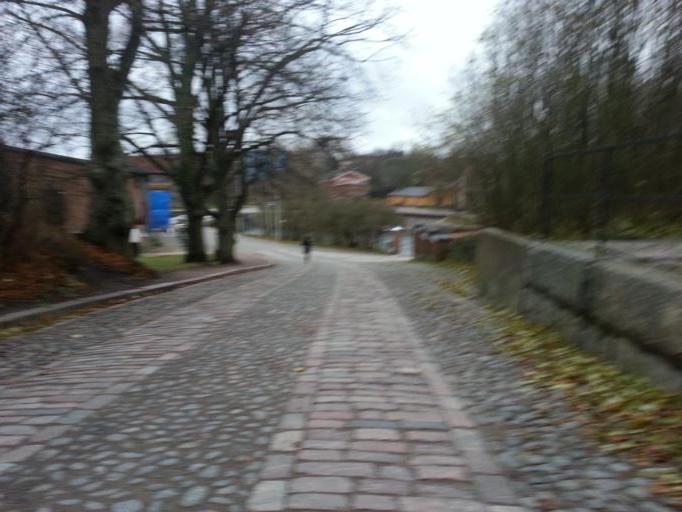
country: FI
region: Uusimaa
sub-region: Helsinki
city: Helsinki
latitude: 60.1460
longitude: 24.9879
